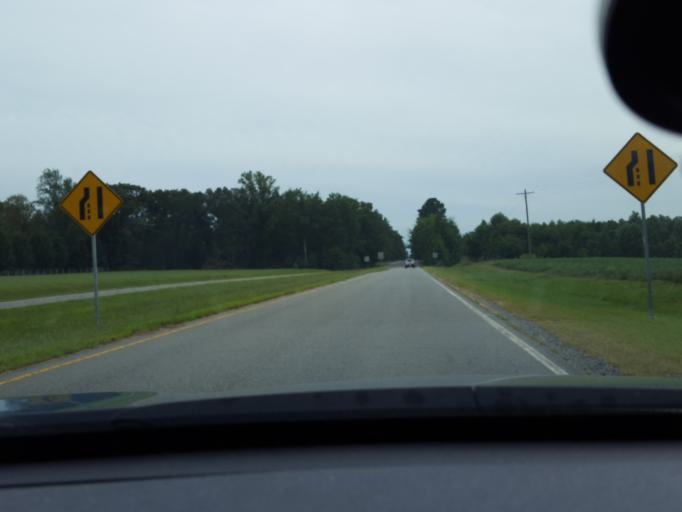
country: US
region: Virginia
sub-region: Caroline County
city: Bowling Green
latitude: 38.0009
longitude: -77.3352
